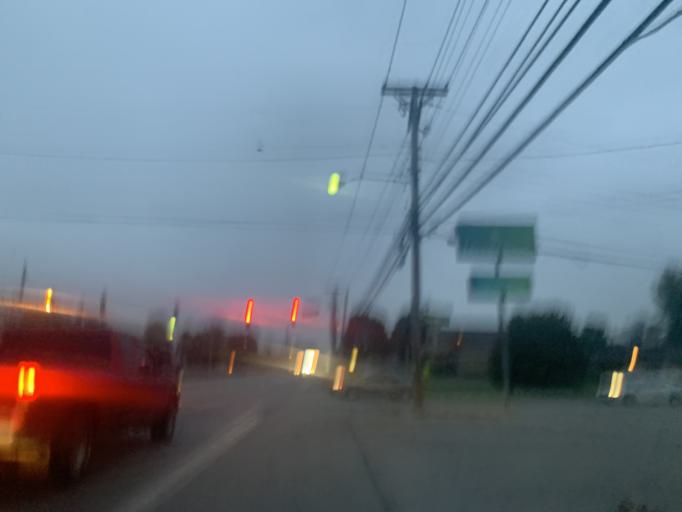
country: US
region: Kentucky
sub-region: Jefferson County
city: Shively
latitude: 38.2162
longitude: -85.7953
